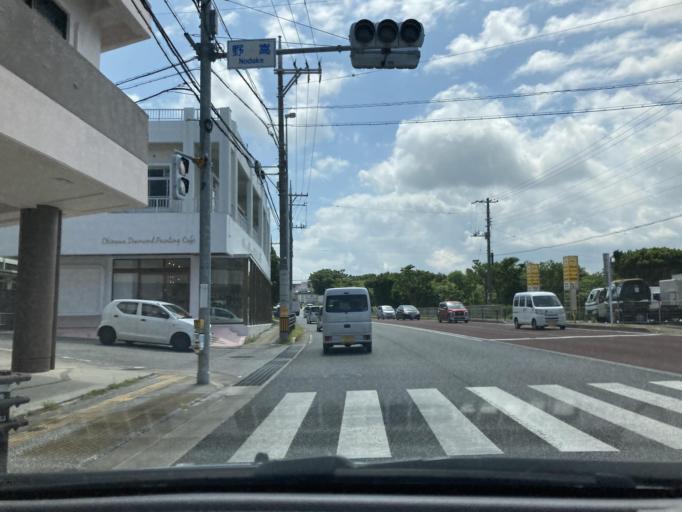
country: JP
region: Okinawa
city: Chatan
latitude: 26.2845
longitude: 127.7764
